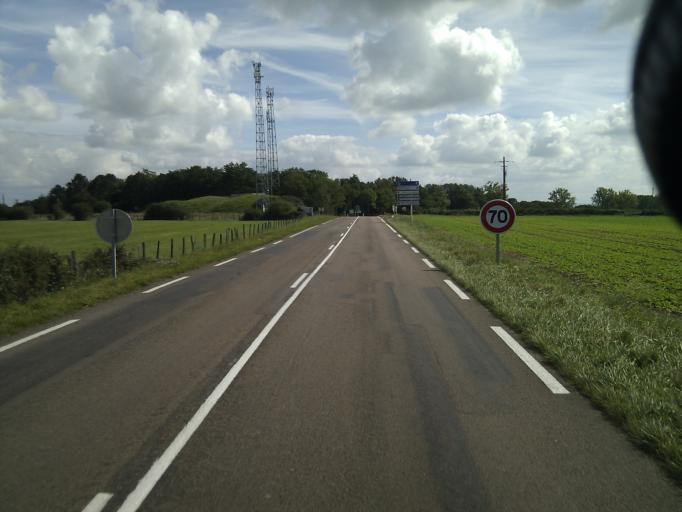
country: FR
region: Bourgogne
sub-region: Departement de la Cote-d'Or
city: Semur-en-Auxois
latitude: 47.4443
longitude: 4.3079
